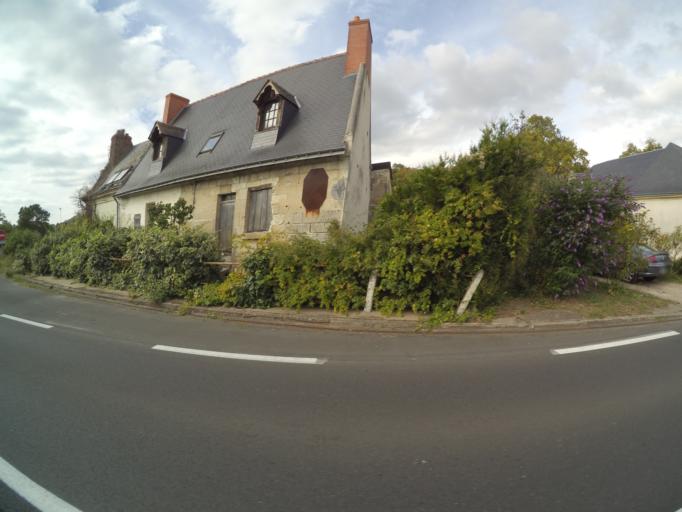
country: FR
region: Centre
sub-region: Departement d'Indre-et-Loire
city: Cinq-Mars-la-Pile
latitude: 47.3536
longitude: 0.4816
